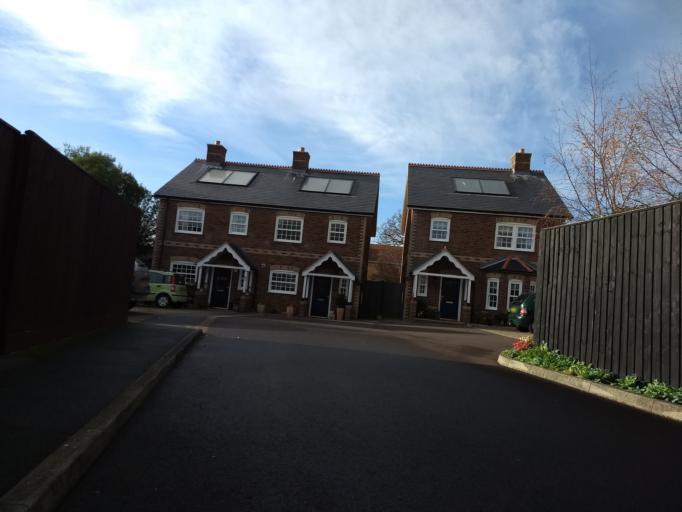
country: GB
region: England
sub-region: Isle of Wight
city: Totland
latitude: 50.6847
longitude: -1.5272
